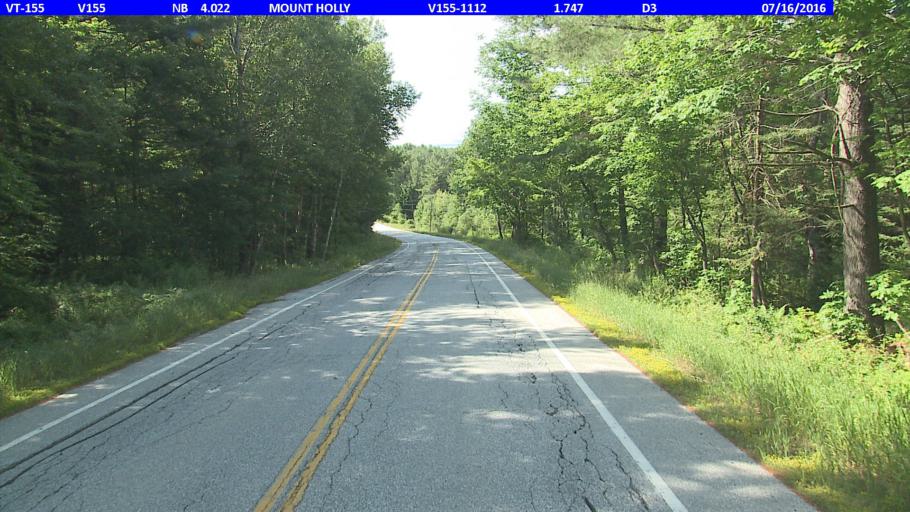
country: US
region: Vermont
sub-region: Windsor County
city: Chester
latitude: 43.3863
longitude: -72.8031
